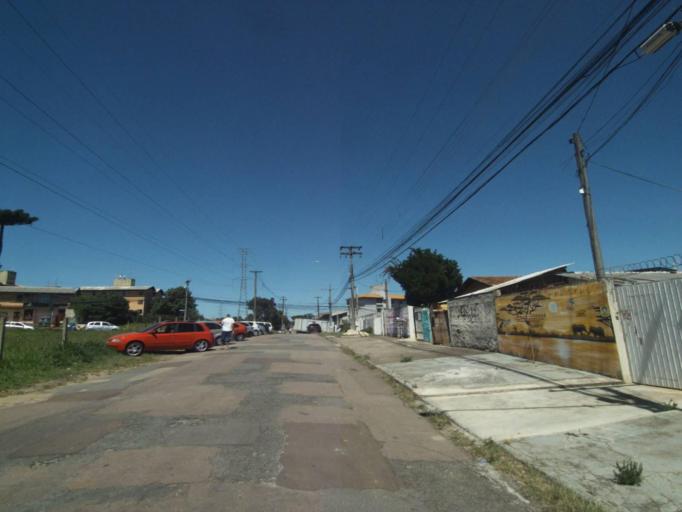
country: BR
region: Parana
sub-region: Curitiba
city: Curitiba
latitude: -25.4746
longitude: -49.3372
